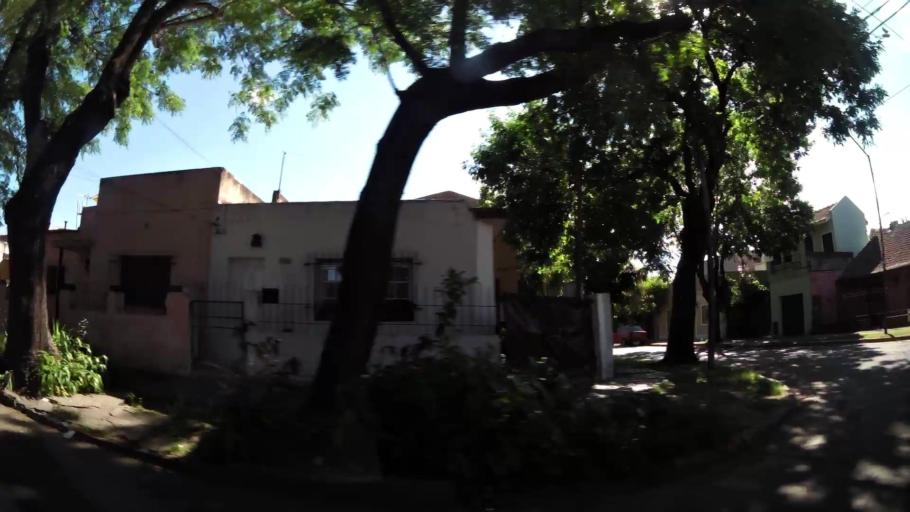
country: AR
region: Buenos Aires
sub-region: Partido de San Isidro
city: San Isidro
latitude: -34.4625
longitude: -58.5362
